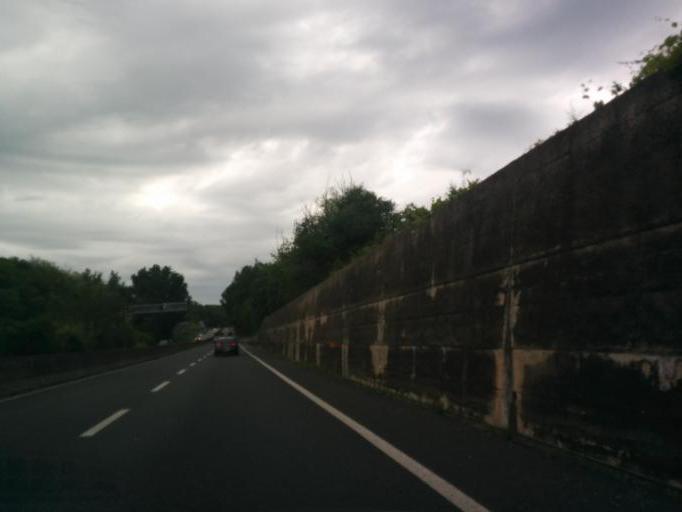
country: IT
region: Tuscany
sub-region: Provincia di Siena
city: Belverde
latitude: 43.3527
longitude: 11.3039
